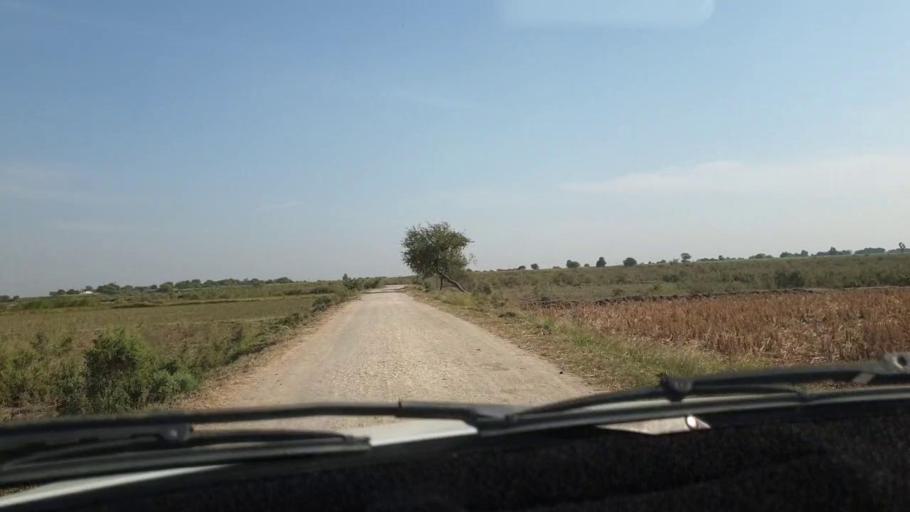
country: PK
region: Sindh
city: Bulri
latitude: 24.9506
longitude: 68.4230
